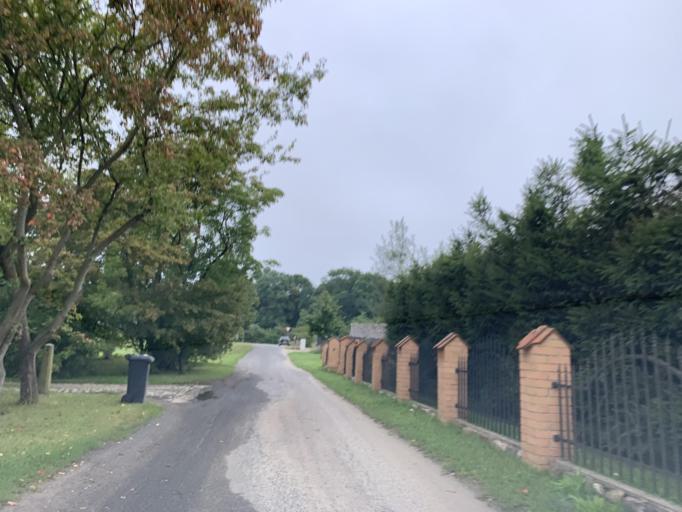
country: DE
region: Mecklenburg-Vorpommern
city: Carpin
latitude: 53.3931
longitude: 13.2301
